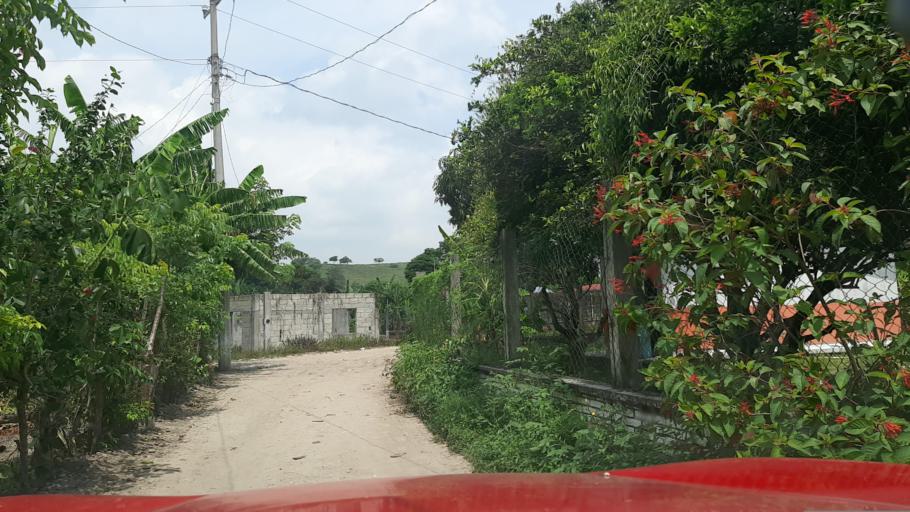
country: MX
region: Veracruz
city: Papantla de Olarte
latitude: 20.4477
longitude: -97.2442
